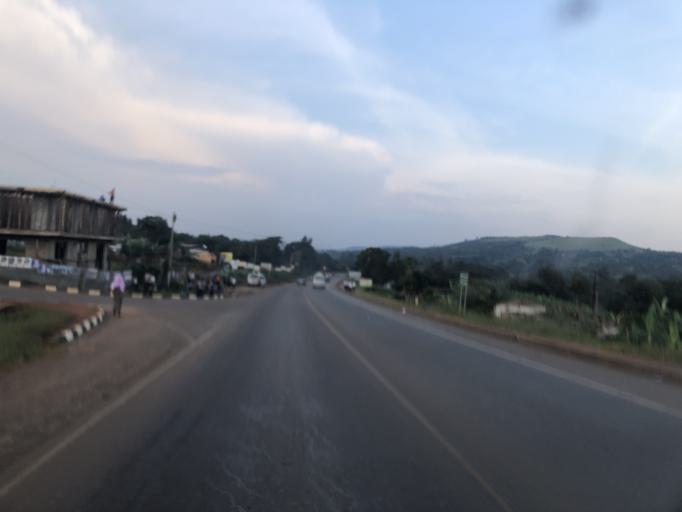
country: UG
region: Central Region
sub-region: Mpigi District
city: Mpigi
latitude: 0.2206
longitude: 32.3347
